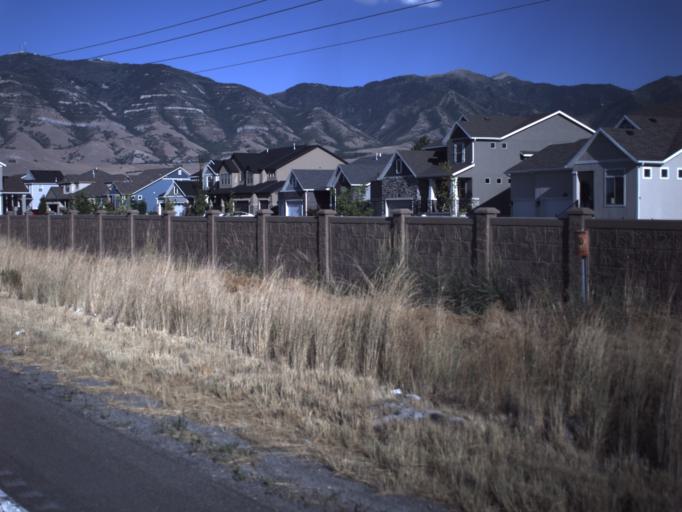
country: US
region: Utah
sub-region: Tooele County
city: Stansbury park
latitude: 40.6458
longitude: -112.3059
